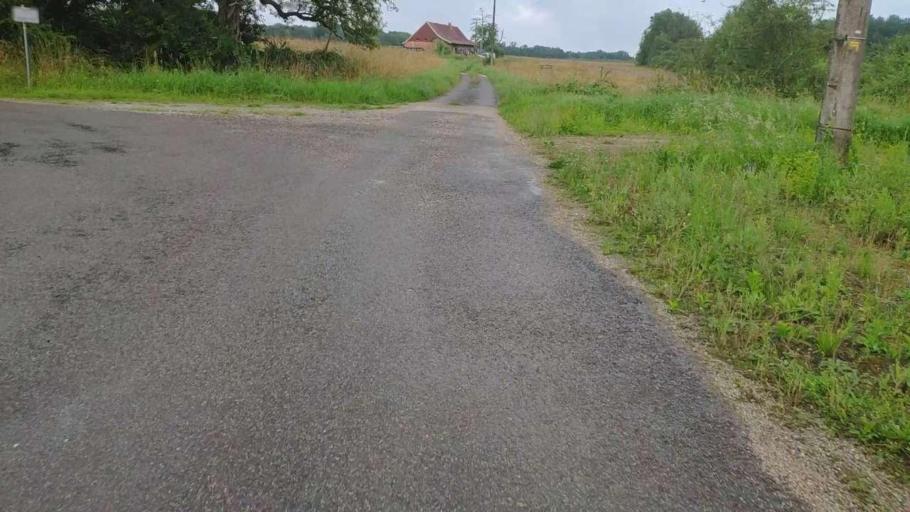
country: FR
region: Franche-Comte
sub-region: Departement du Jura
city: Mont-sous-Vaudrey
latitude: 46.8643
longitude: 5.5360
